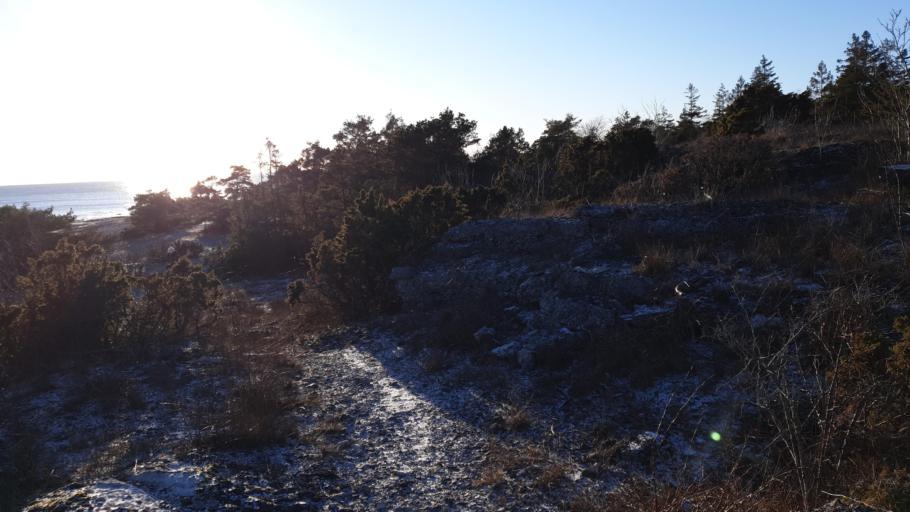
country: SE
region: Gotland
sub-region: Gotland
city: Slite
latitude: 57.3731
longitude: 18.8112
